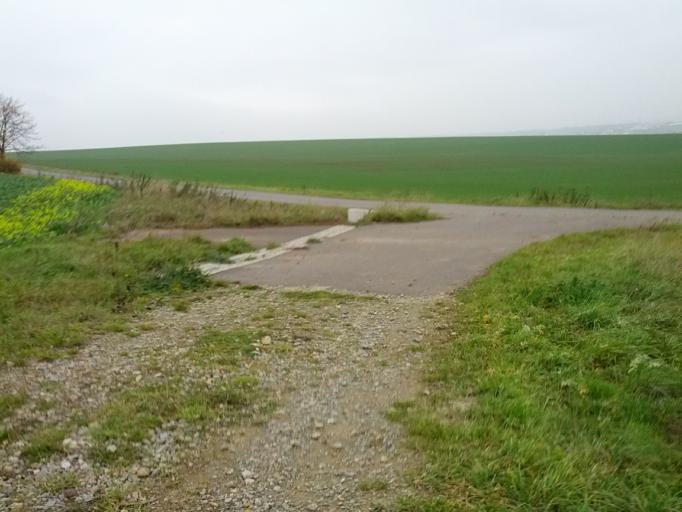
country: DE
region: Thuringia
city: Seebach
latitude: 50.9727
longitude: 10.4201
